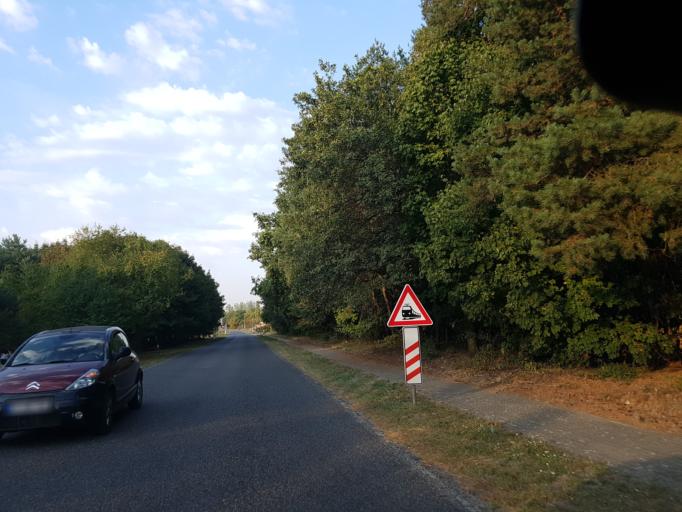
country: DE
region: Brandenburg
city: Hohenleipisch
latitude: 51.4752
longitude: 13.5746
